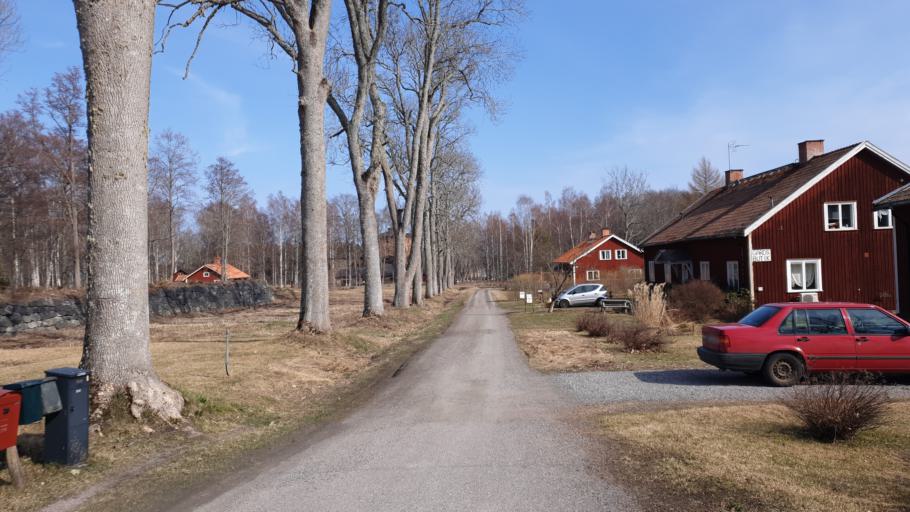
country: SE
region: Gaevleborg
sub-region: Gavle Kommun
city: Norrsundet
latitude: 61.0465
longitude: 17.1448
